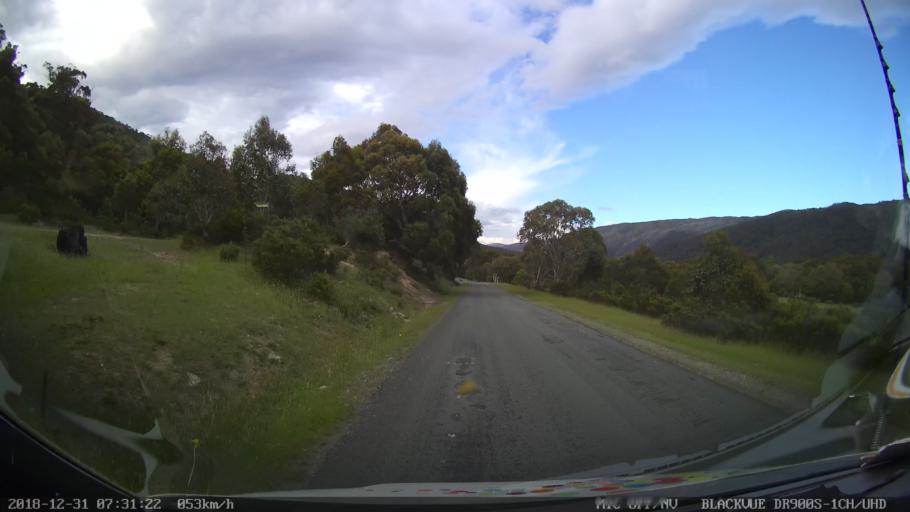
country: AU
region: New South Wales
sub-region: Snowy River
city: Jindabyne
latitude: -36.3256
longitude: 148.4738
